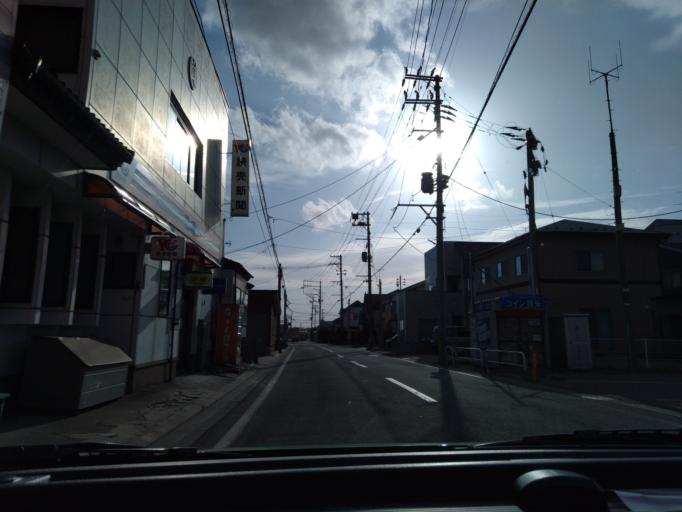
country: JP
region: Akita
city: Akita Shi
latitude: 39.7651
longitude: 140.0731
